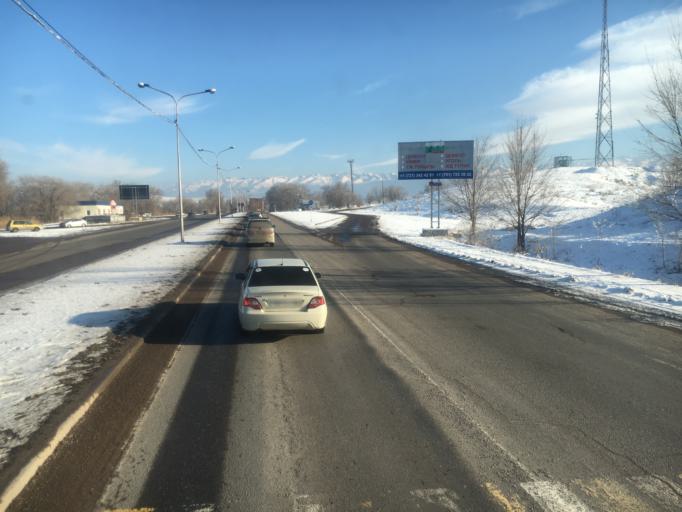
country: KZ
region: Almaty Oblysy
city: Burunday
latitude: 43.2774
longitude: 76.2864
